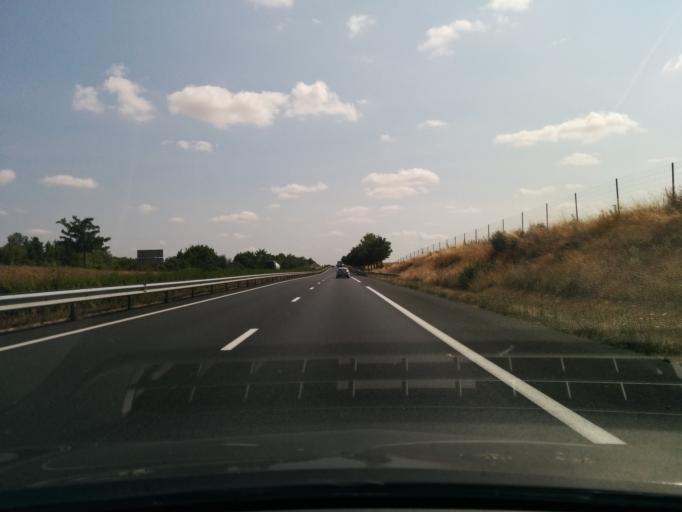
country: FR
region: Centre
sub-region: Departement de l'Indre
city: Vatan
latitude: 47.0363
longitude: 1.7929
